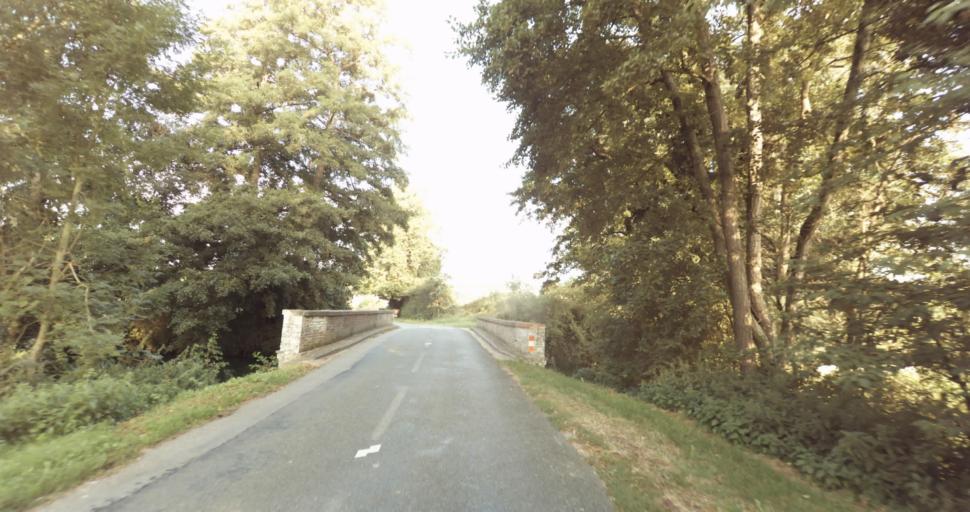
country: FR
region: Centre
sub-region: Departement d'Eure-et-Loir
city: Vert-en-Drouais
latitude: 48.7754
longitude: 1.3398
